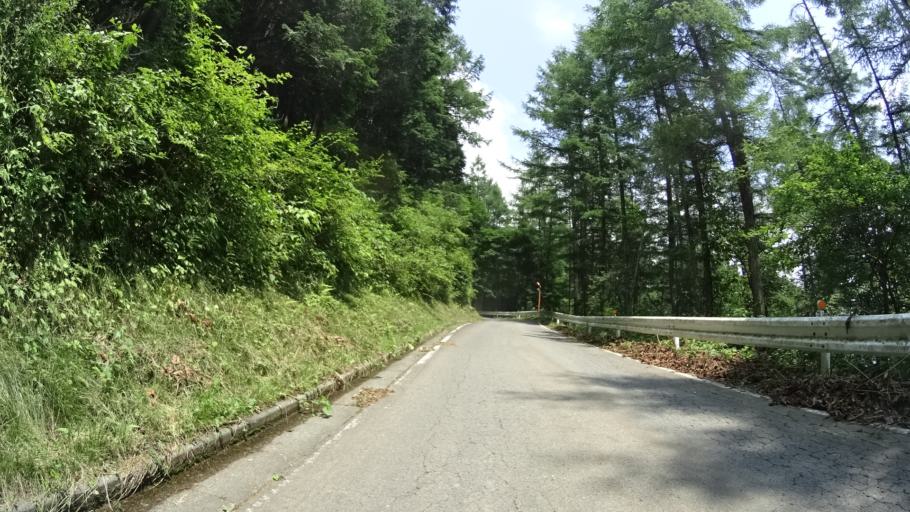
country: JP
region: Nagano
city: Saku
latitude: 36.1031
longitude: 138.6464
